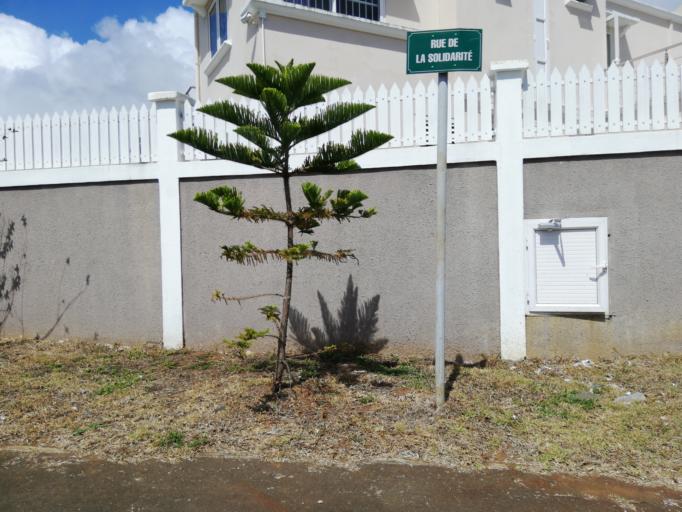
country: MU
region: Plaines Wilhems
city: Ebene
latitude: -20.2371
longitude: 57.4825
